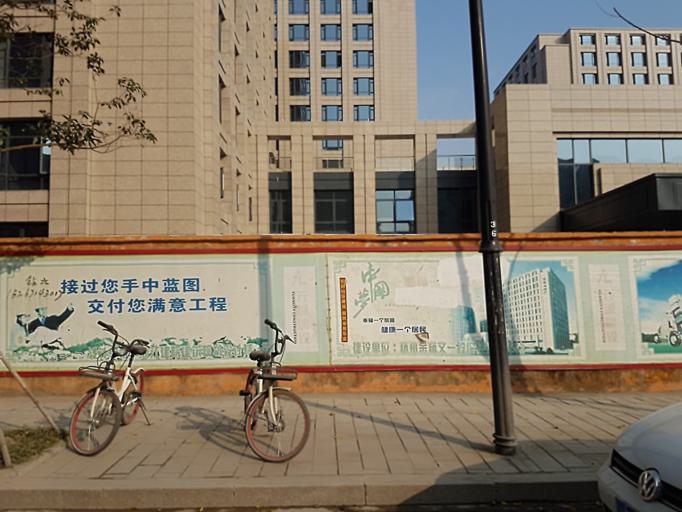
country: CN
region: Zhejiang Sheng
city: Jiangcun
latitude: 30.2963
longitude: 120.0406
